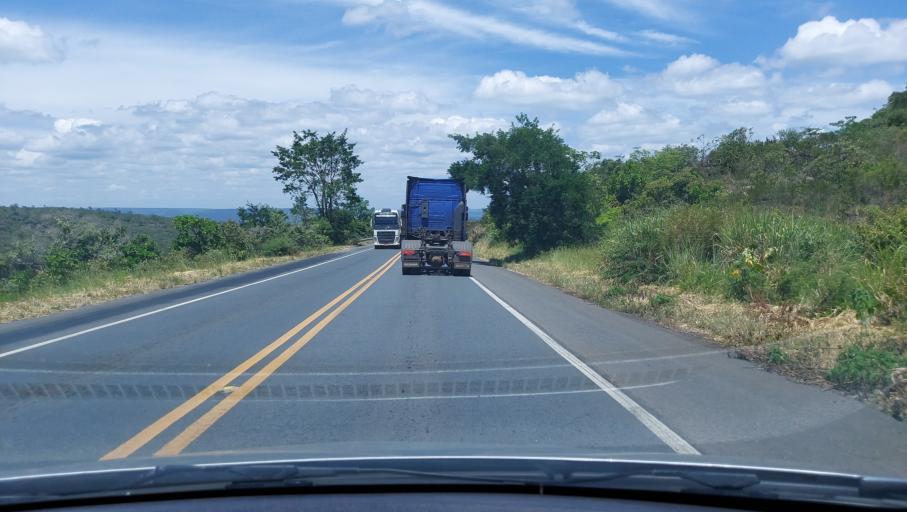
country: BR
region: Bahia
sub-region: Iraquara
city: Iraquara
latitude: -12.4660
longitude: -41.4097
